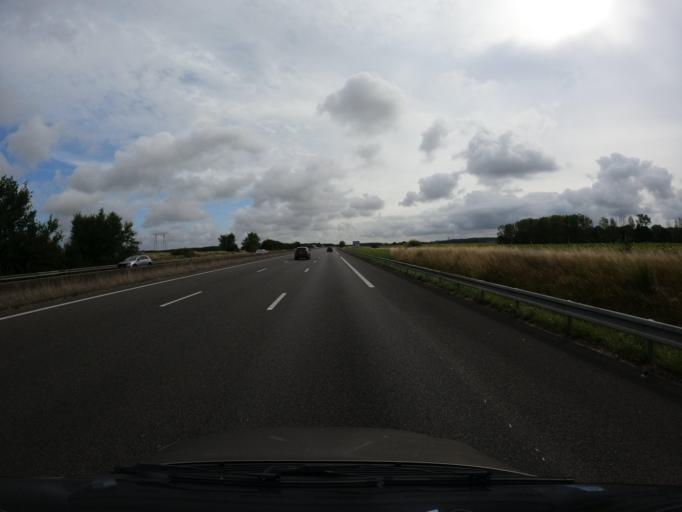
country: FR
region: Centre
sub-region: Departement du Loir-et-Cher
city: Herbault
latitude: 47.5993
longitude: 1.1048
